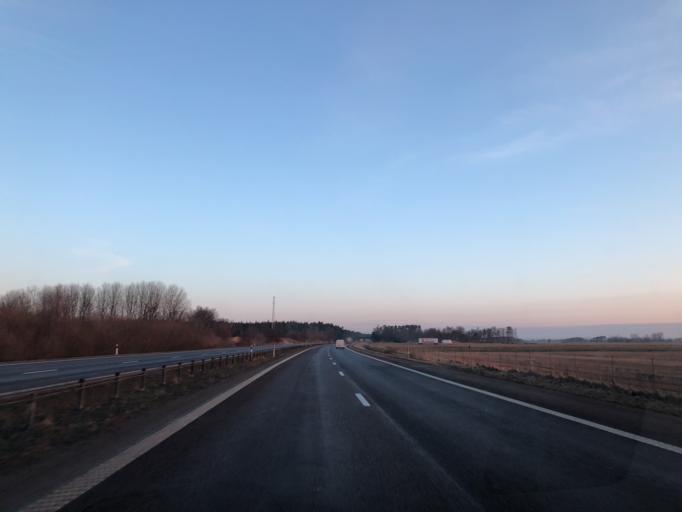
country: SE
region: Halland
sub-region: Laholms Kommun
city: Mellbystrand
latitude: 56.4709
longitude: 12.9420
